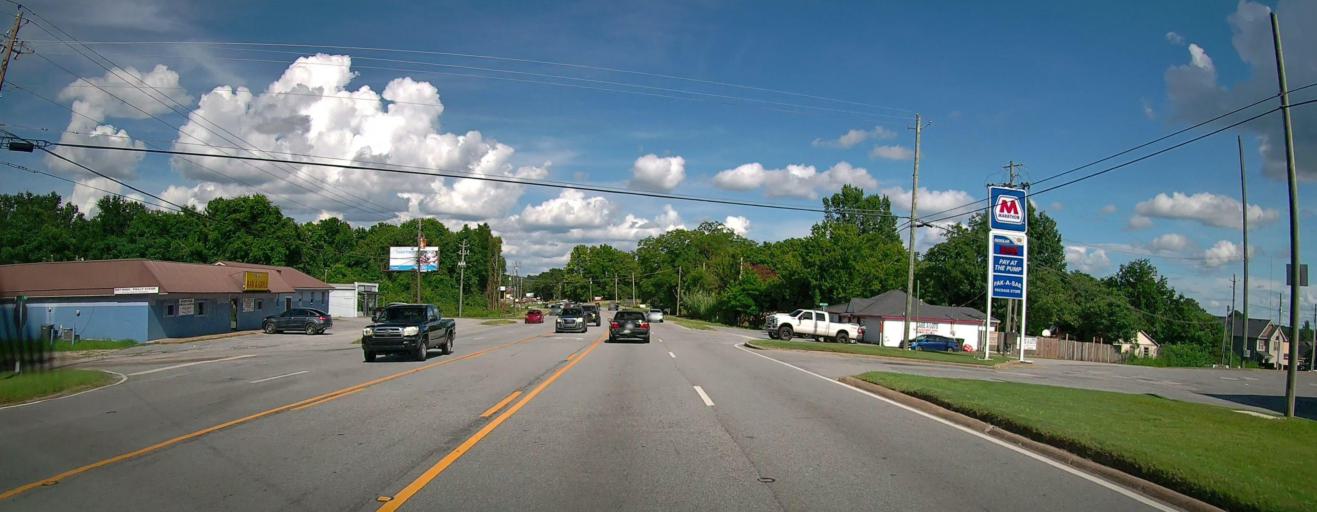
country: US
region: Alabama
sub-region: Russell County
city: Ladonia
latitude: 32.4683
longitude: -85.0791
